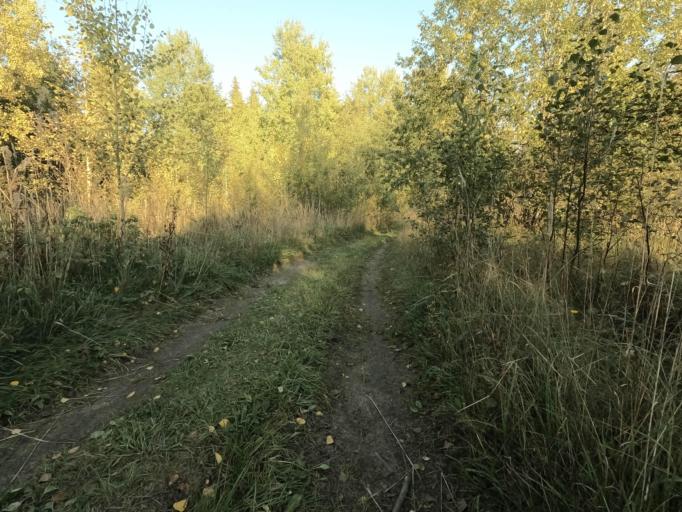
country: RU
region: Leningrad
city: Nikol'skoye
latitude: 59.7010
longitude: 30.7426
